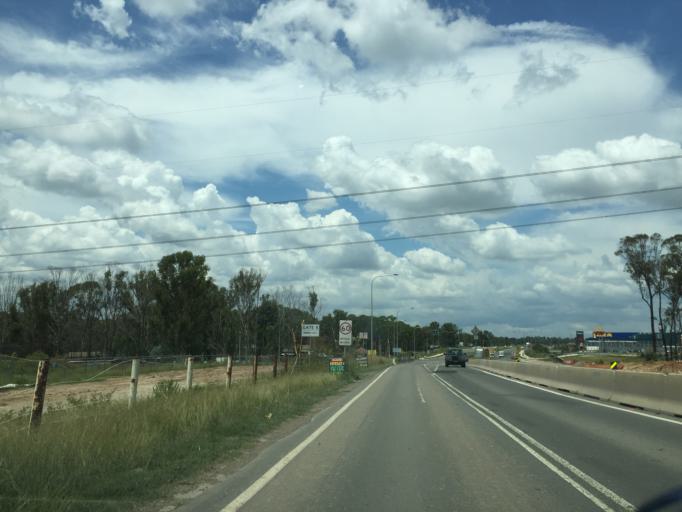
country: AU
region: New South Wales
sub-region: Blacktown
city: Hassall Grove
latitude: -33.7128
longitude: 150.8425
